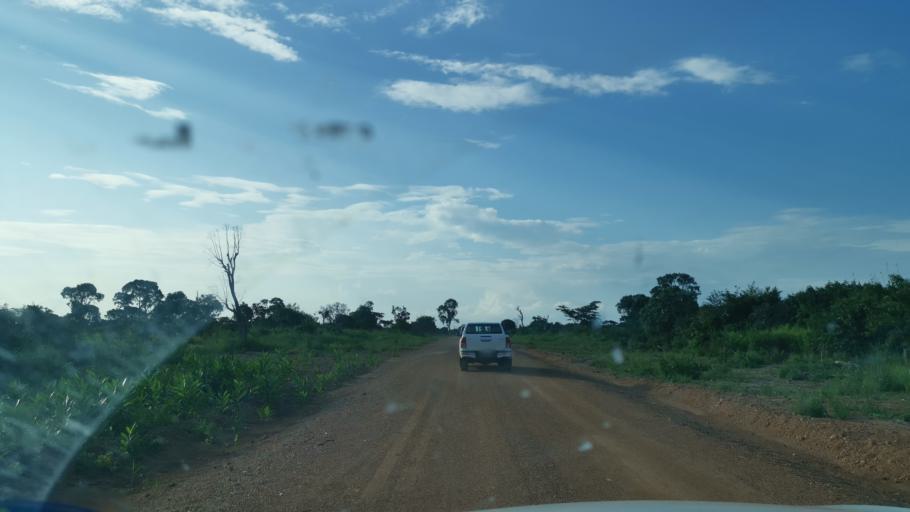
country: ZM
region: Luapula
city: Samfya
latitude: -11.1190
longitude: 29.5798
